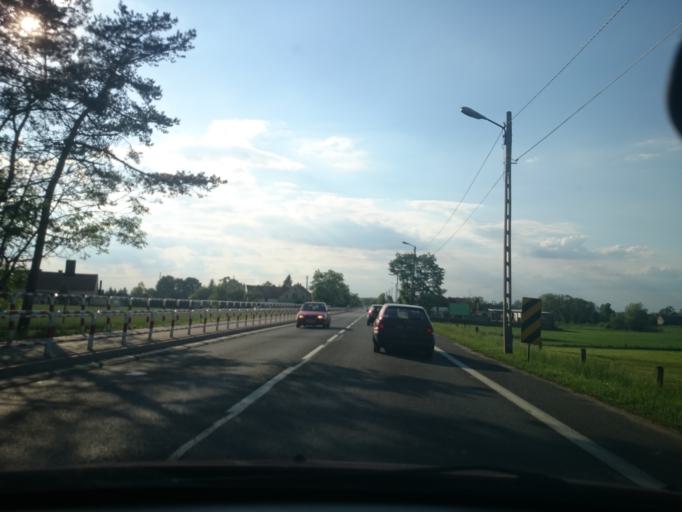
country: PL
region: Opole Voivodeship
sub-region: Powiat strzelecki
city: Izbicko
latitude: 50.5507
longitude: 18.2256
